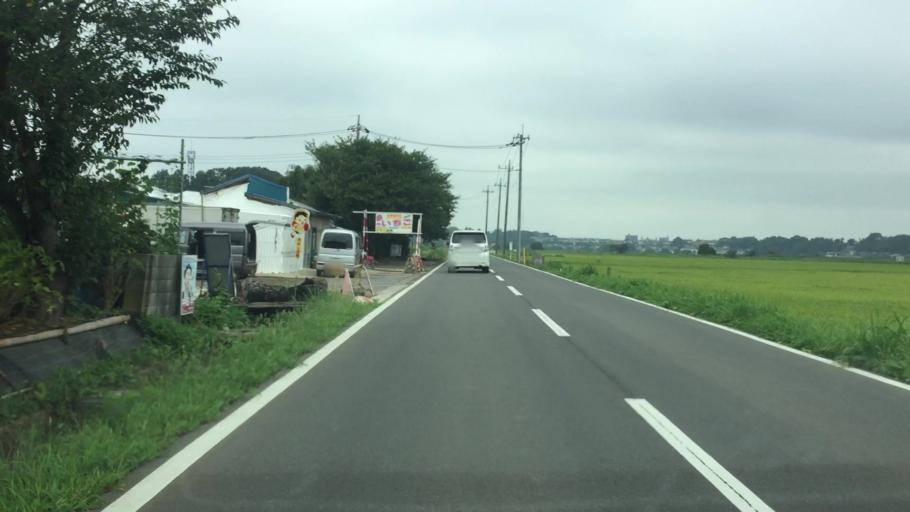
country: JP
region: Chiba
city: Abiko
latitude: 35.8486
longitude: 140.0482
